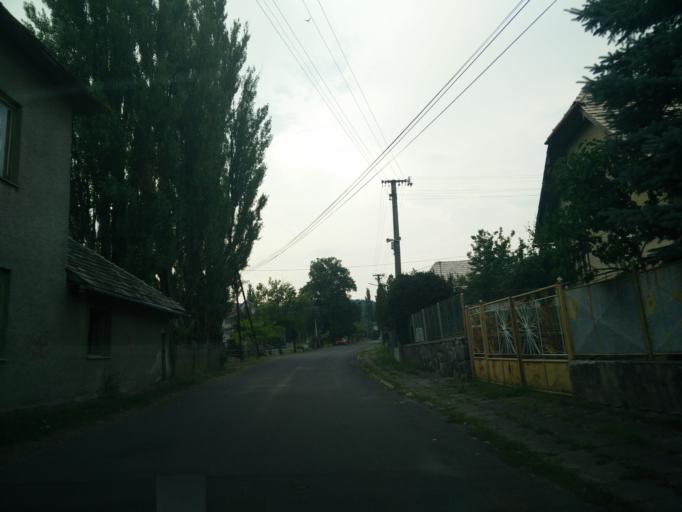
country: SK
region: Nitriansky
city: Handlova
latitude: 48.6526
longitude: 18.7862
